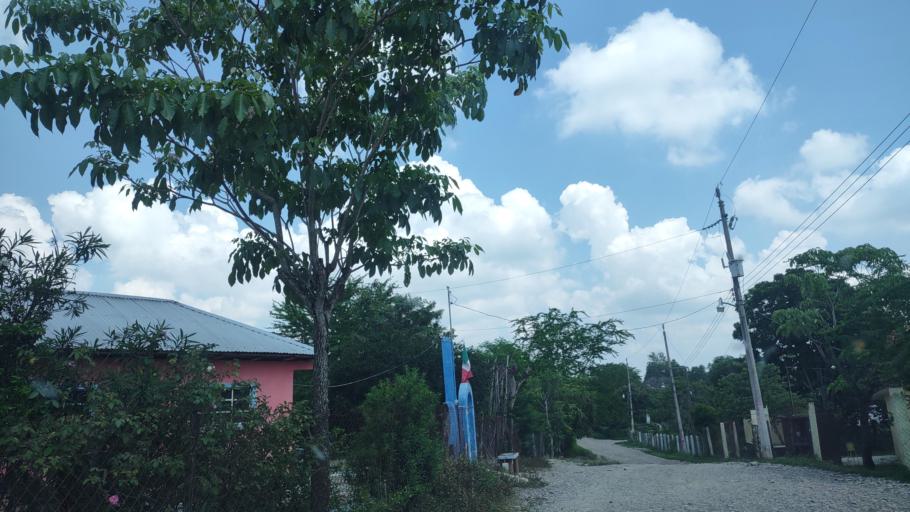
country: MX
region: Veracruz
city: Tempoal de Sanchez
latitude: 21.5457
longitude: -98.2765
